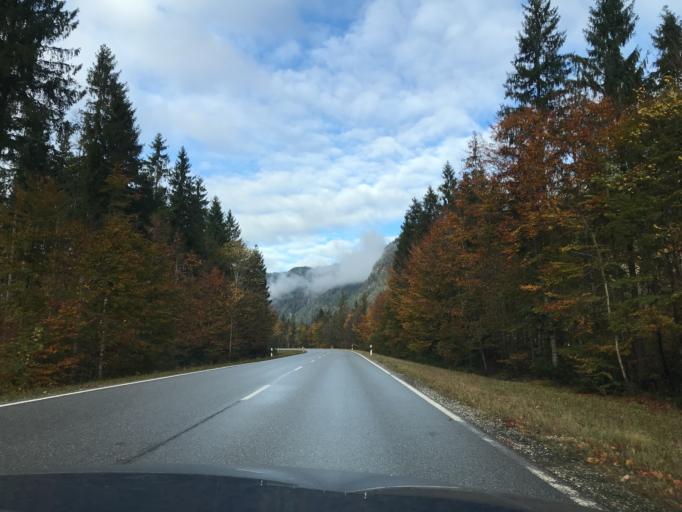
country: DE
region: Bavaria
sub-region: Upper Bavaria
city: Jachenau
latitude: 47.5588
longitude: 11.4739
